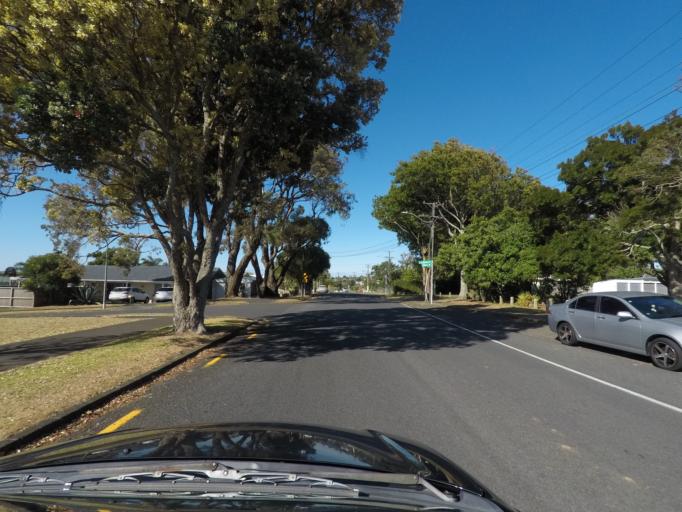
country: NZ
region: Auckland
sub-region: Auckland
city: Rosebank
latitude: -36.8863
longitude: 174.6869
